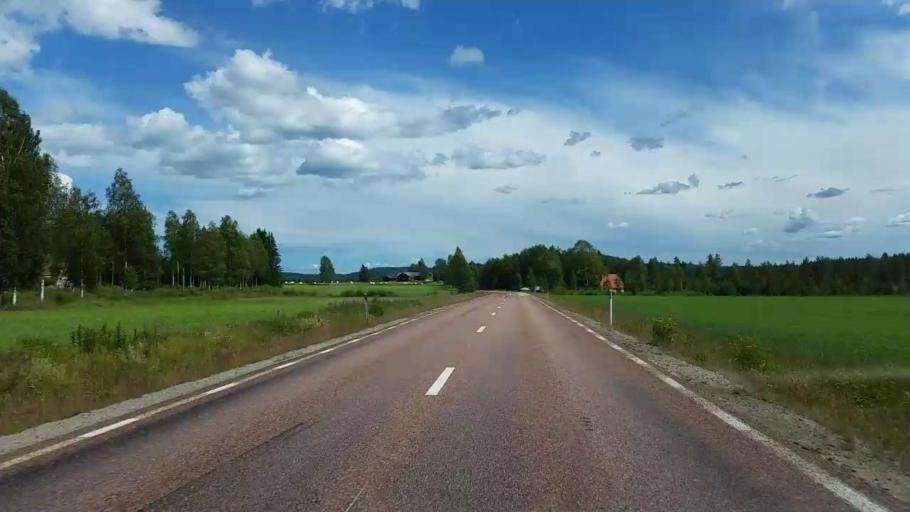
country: SE
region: Gaevleborg
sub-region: Ovanakers Kommun
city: Edsbyn
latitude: 61.3463
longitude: 15.6234
